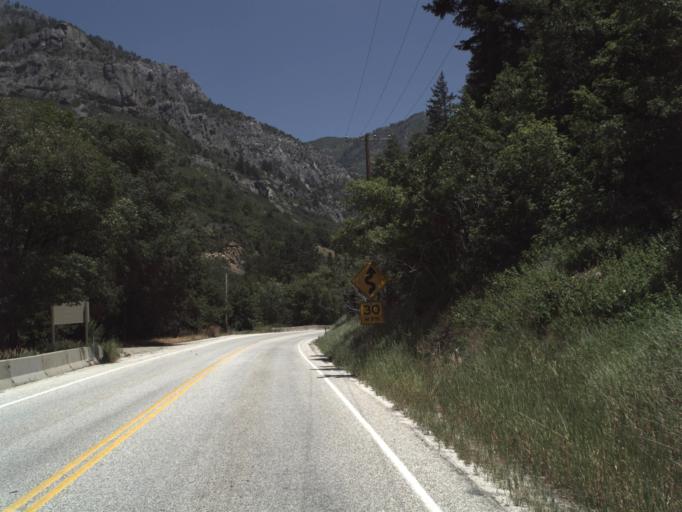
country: US
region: Utah
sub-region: Weber County
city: Ogden
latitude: 41.2458
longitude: -111.8920
